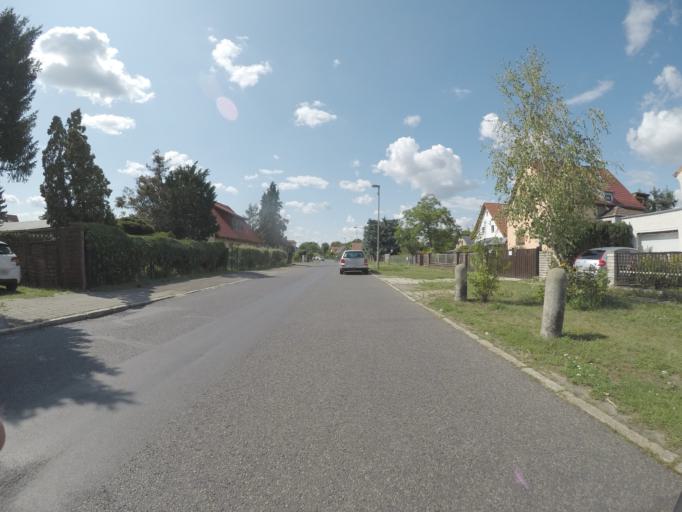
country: DE
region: Berlin
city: Mahlsdorf
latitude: 52.5106
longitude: 13.6017
